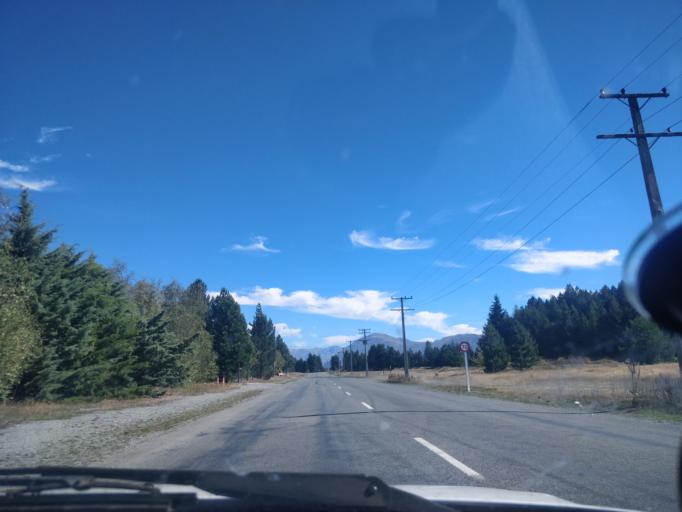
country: NZ
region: Otago
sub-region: Queenstown-Lakes District
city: Wanaka
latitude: -44.2648
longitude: 170.0861
